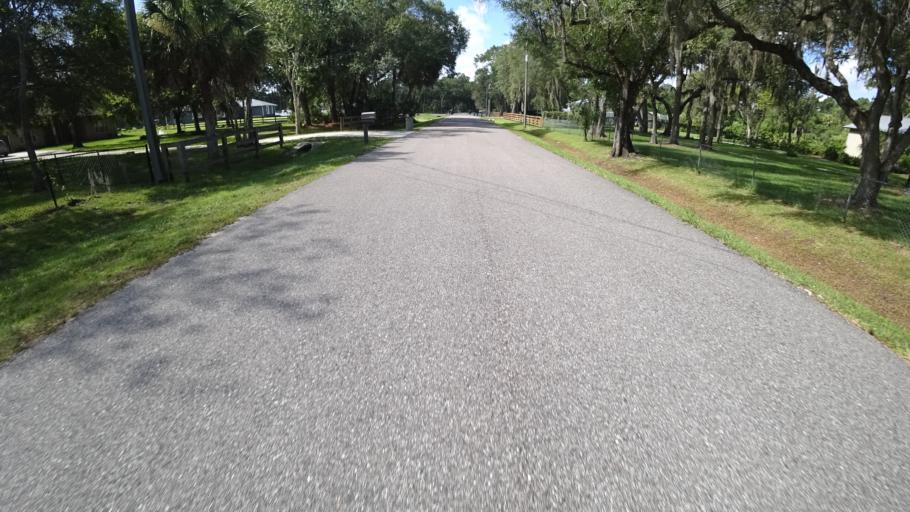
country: US
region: Florida
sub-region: Manatee County
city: Ellenton
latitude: 27.4866
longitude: -82.4855
